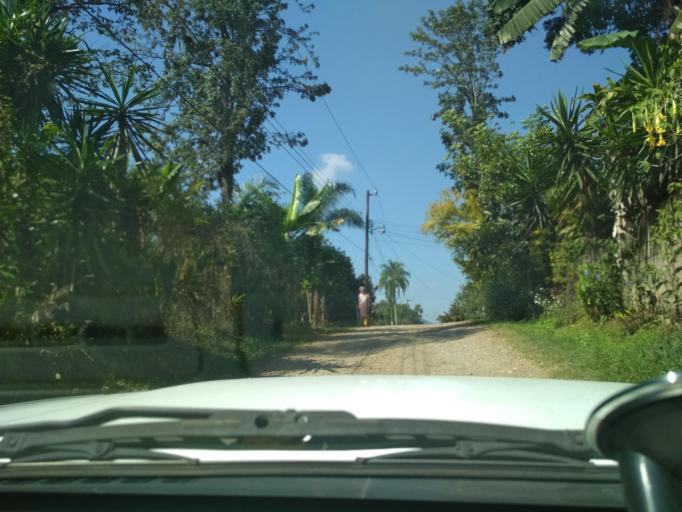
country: MX
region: Veracruz
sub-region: Fortin
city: Fraccionamiento los Alamos
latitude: 18.9186
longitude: -96.9814
